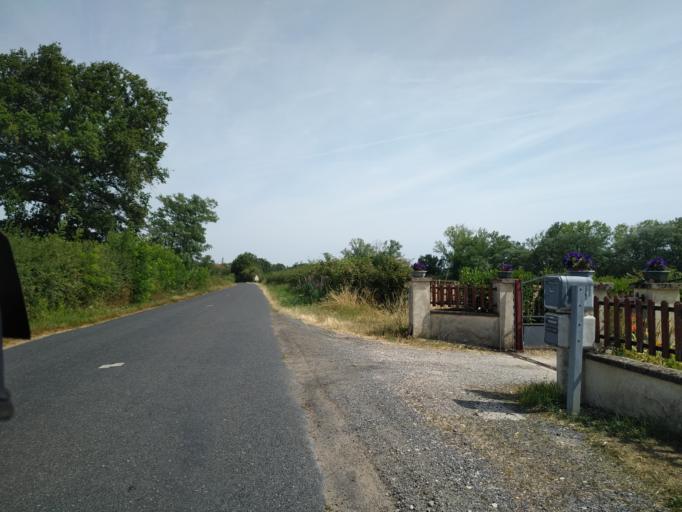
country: FR
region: Auvergne
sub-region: Departement de l'Allier
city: Molinet
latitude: 46.4187
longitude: 3.9765
